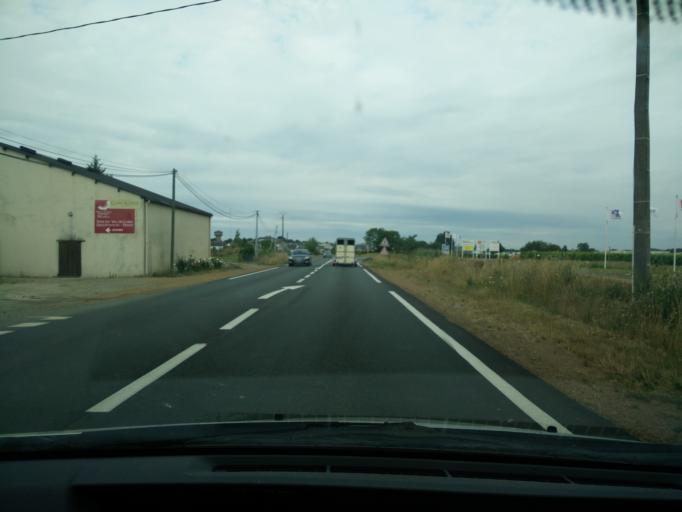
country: FR
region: Pays de la Loire
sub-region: Departement de Maine-et-Loire
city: Brissac-Quince
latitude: 47.3419
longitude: -0.4349
